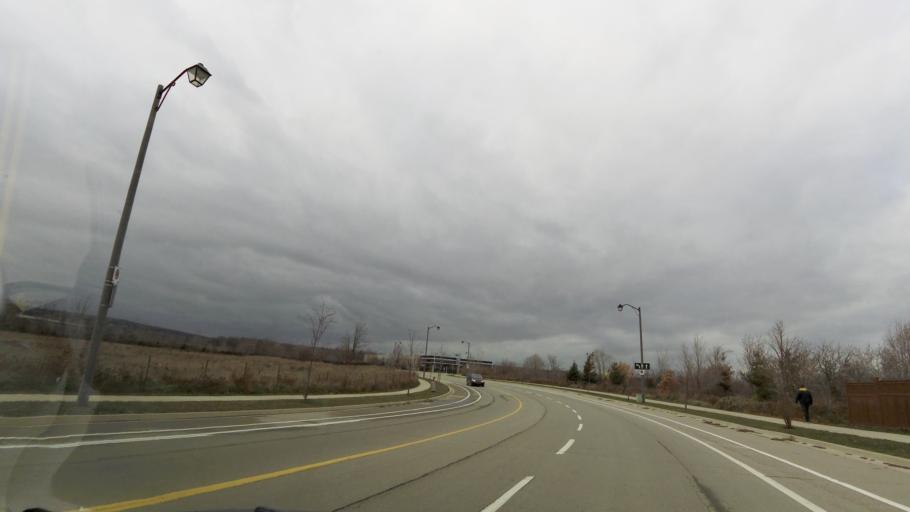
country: CA
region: Ontario
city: Burlington
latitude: 43.3977
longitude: -79.8287
